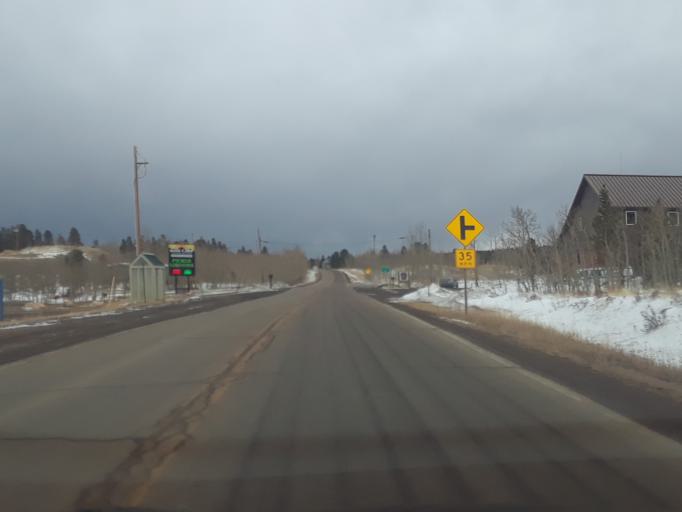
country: US
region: Colorado
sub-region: Gilpin County
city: Central City
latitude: 39.8406
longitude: -105.4820
